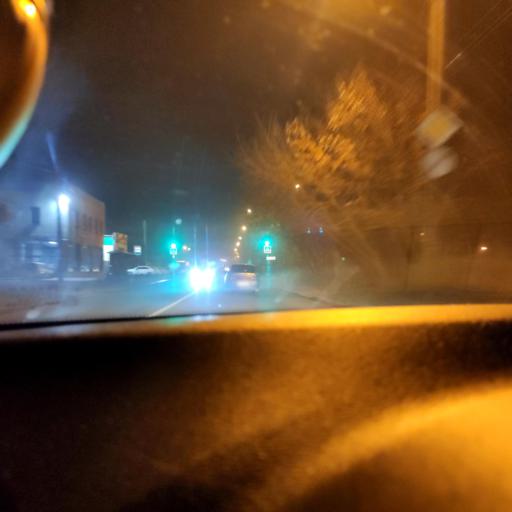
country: RU
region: Samara
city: Smyshlyayevka
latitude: 53.2461
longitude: 50.3471
